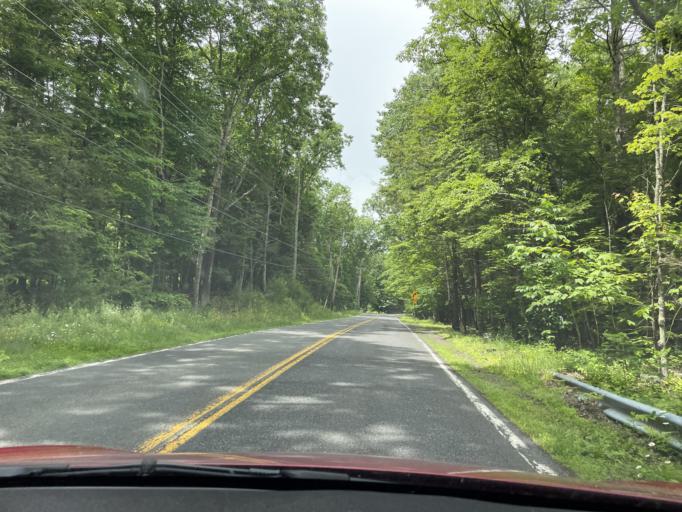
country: US
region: New York
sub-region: Ulster County
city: Zena
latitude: 42.0053
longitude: -74.0666
